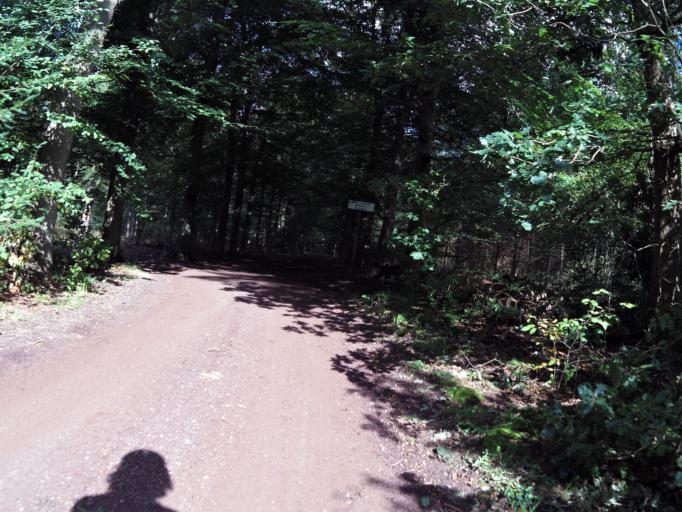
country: NL
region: Utrecht
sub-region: Gemeente Soest
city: Soest
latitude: 52.1794
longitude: 5.2459
